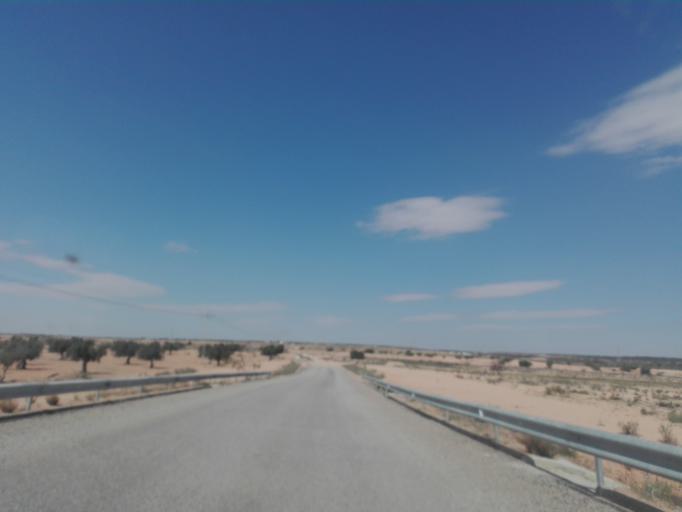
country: TN
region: Safaqis
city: Sfax
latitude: 34.6868
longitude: 10.5521
